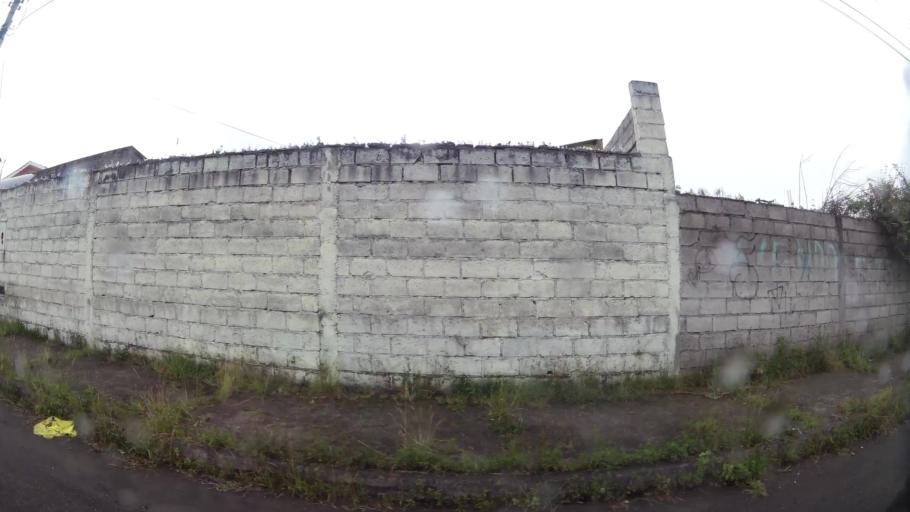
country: EC
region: Pichincha
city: Sangolqui
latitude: -0.2874
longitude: -78.4637
